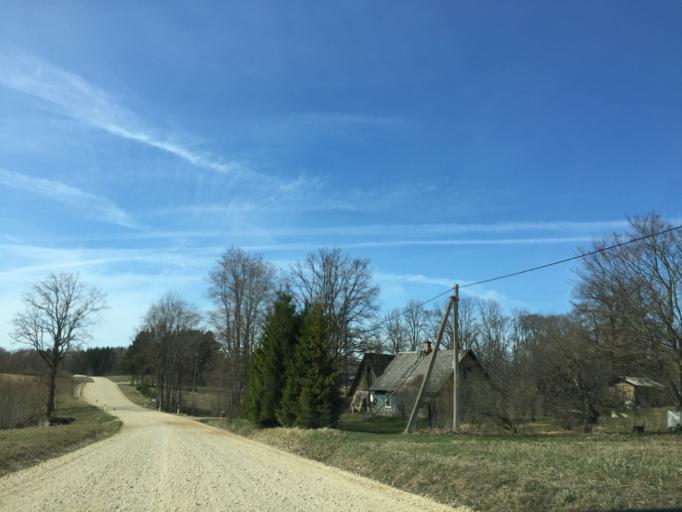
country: EE
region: Vorumaa
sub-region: Antsla vald
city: Vana-Antsla
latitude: 57.9563
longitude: 26.3552
